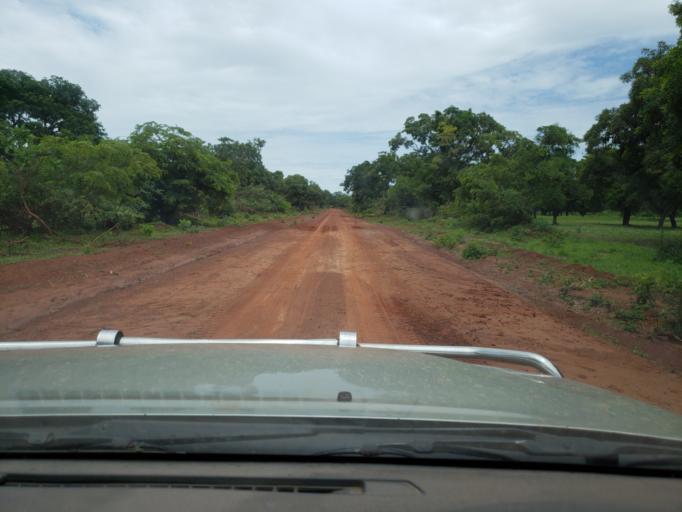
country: ML
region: Sikasso
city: Sikasso
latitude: 11.6611
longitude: -6.3421
